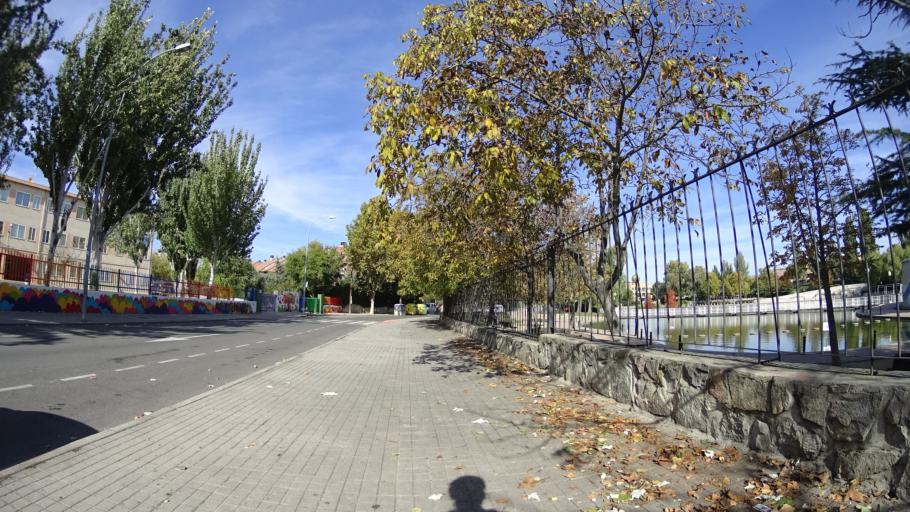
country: ES
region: Madrid
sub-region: Provincia de Madrid
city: Collado-Villalba
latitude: 40.6221
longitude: -4.0181
